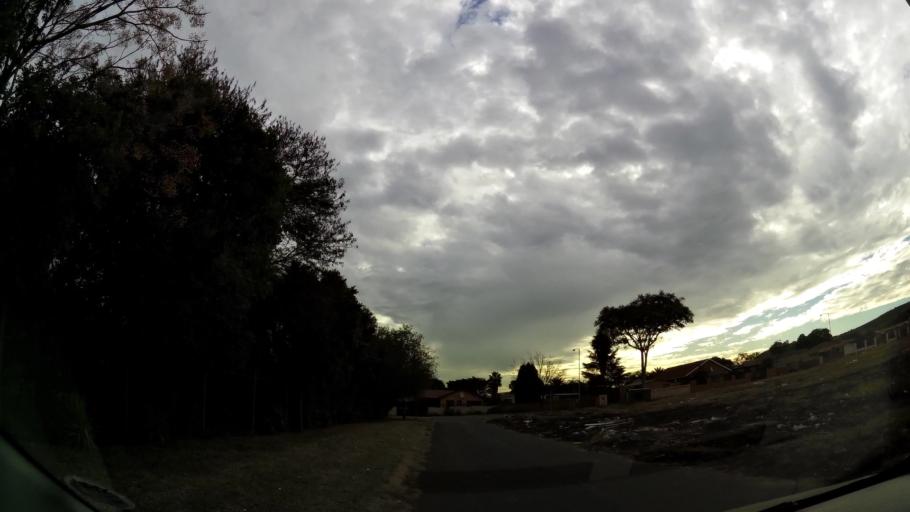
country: ZA
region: Gauteng
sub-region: City of Tshwane Metropolitan Municipality
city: Pretoria
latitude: -25.7021
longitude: 28.3106
